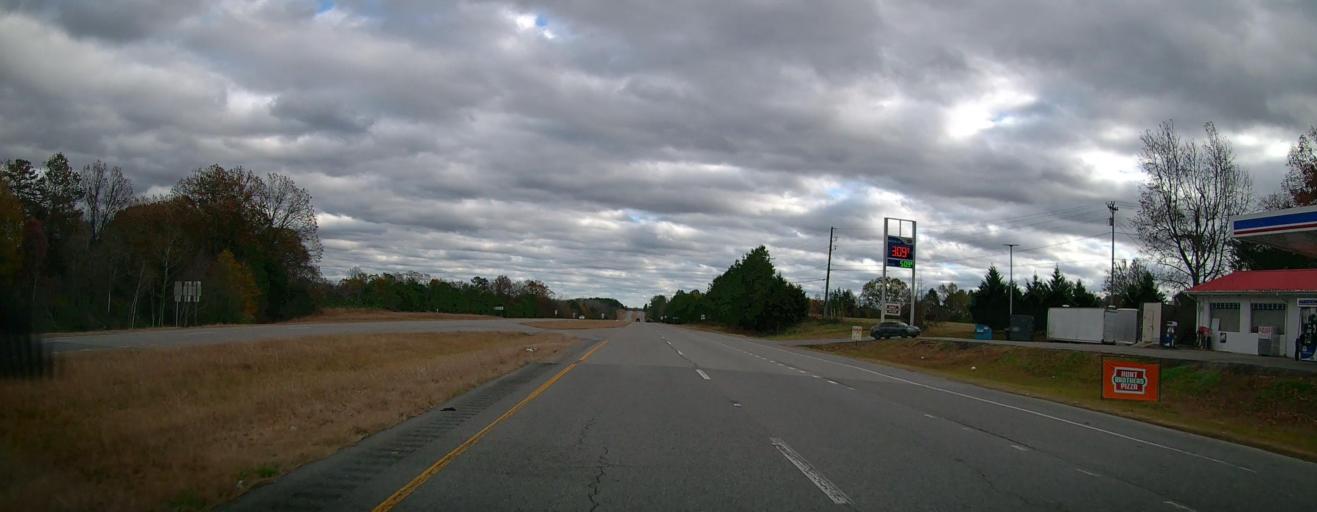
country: US
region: Alabama
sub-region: Lawrence County
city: Town Creek
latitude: 34.5886
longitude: -87.4236
